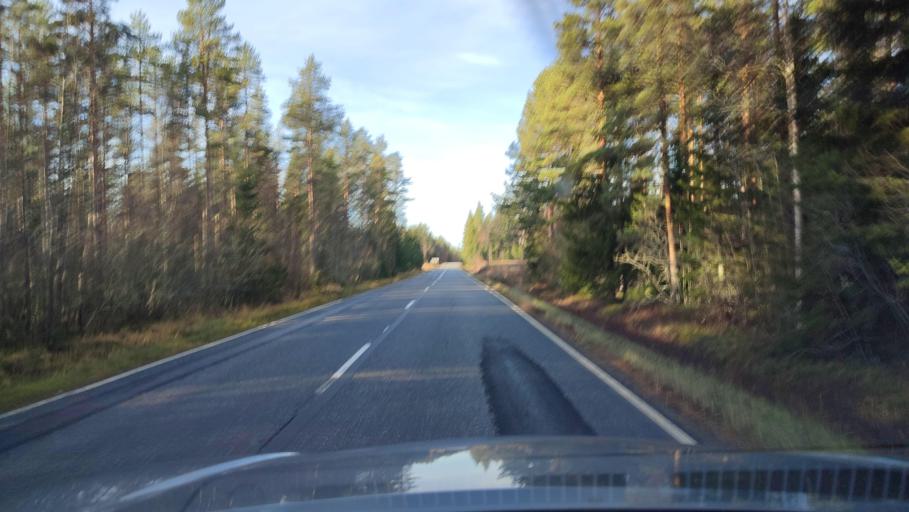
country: FI
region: Southern Ostrobothnia
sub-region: Suupohja
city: Teuva
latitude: 62.4593
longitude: 21.5600
